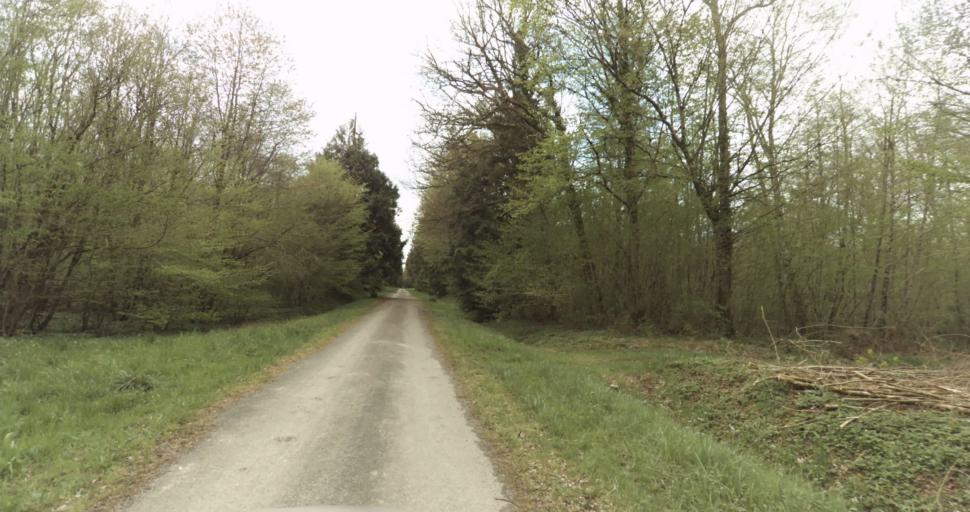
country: FR
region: Bourgogne
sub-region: Departement de la Cote-d'Or
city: Auxonne
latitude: 47.1662
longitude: 5.4234
